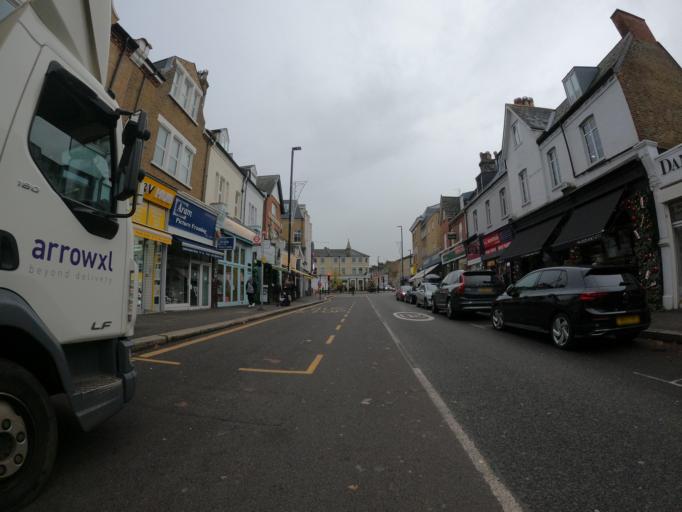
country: GB
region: England
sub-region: Greater London
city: Acton
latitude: 51.4934
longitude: -0.2552
